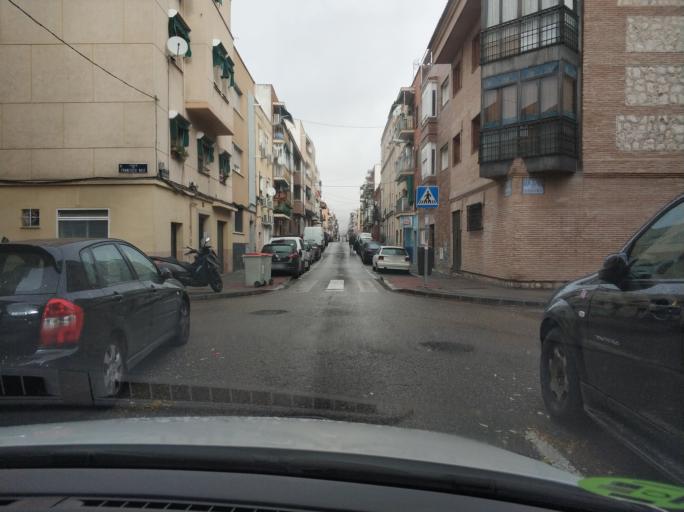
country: ES
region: Madrid
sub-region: Provincia de Madrid
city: Usera
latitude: 40.3818
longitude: -3.7050
